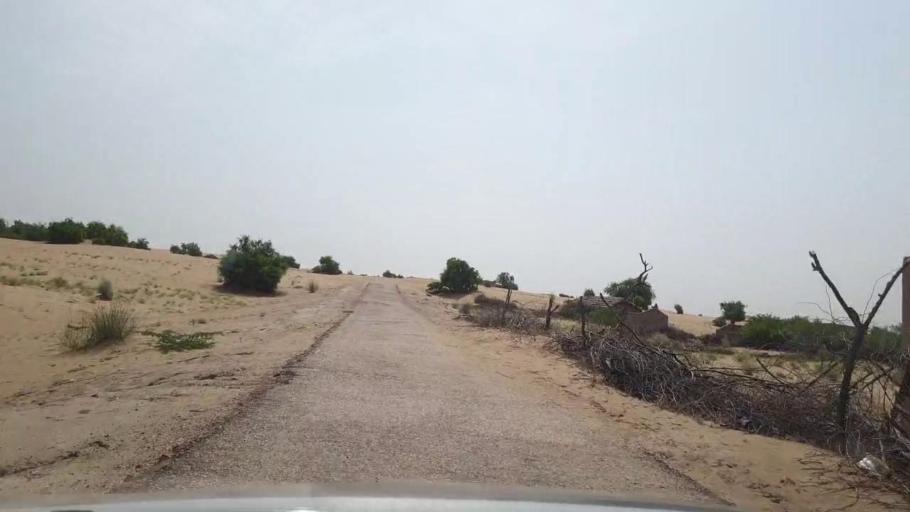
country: PK
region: Sindh
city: Pano Aqil
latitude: 27.6108
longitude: 69.1462
